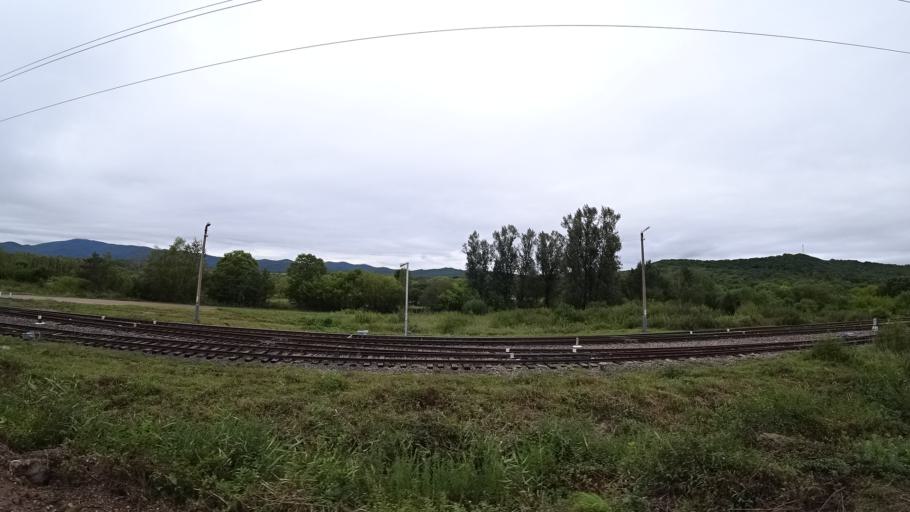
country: RU
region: Primorskiy
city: Rettikhovka
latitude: 44.1629
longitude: 132.7408
